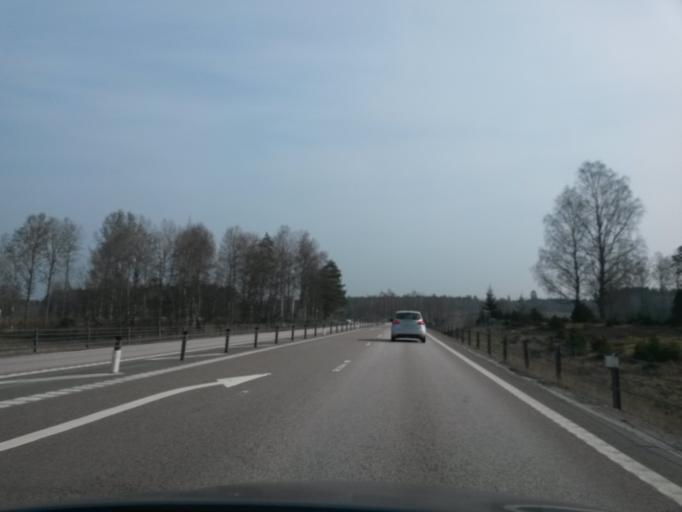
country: SE
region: Vaestra Goetaland
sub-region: Toreboda Kommun
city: Toereboda
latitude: 58.7641
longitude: 13.9768
